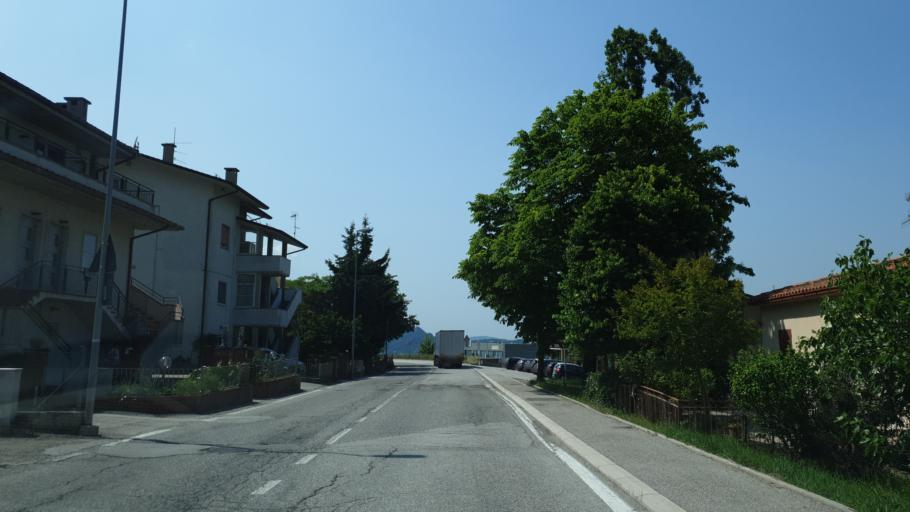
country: SM
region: Acquaviva
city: Acquaviva
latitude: 43.9465
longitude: 12.4272
